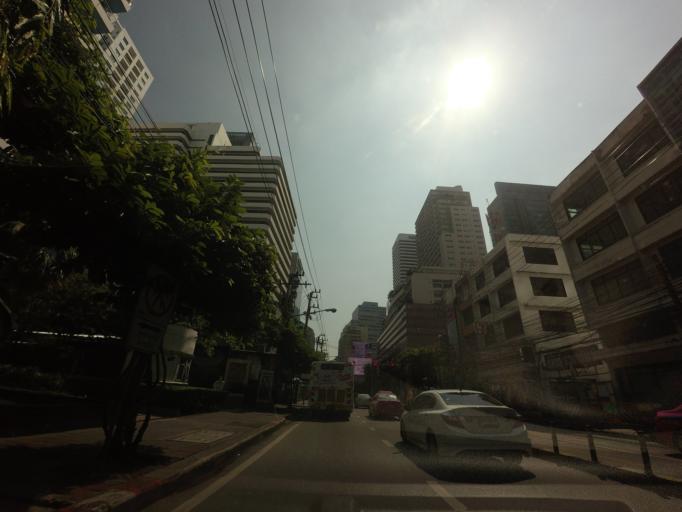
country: TH
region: Bangkok
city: Din Daeng
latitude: 13.7447
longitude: 100.5625
